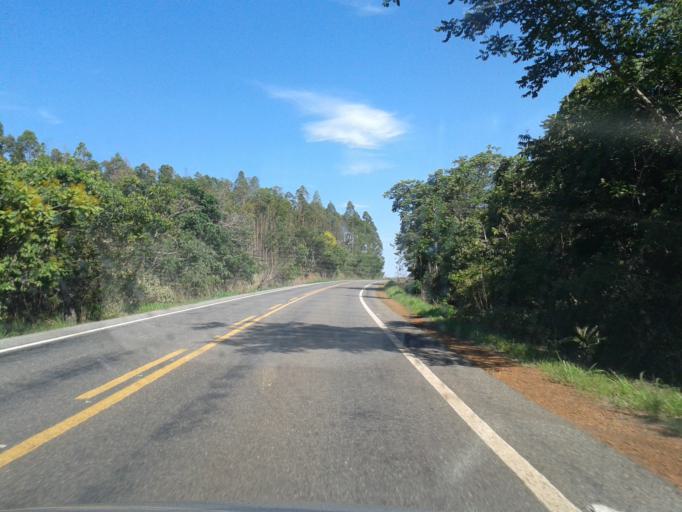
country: BR
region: Goias
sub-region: Piracanjuba
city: Piracanjuba
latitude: -17.3292
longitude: -48.8005
